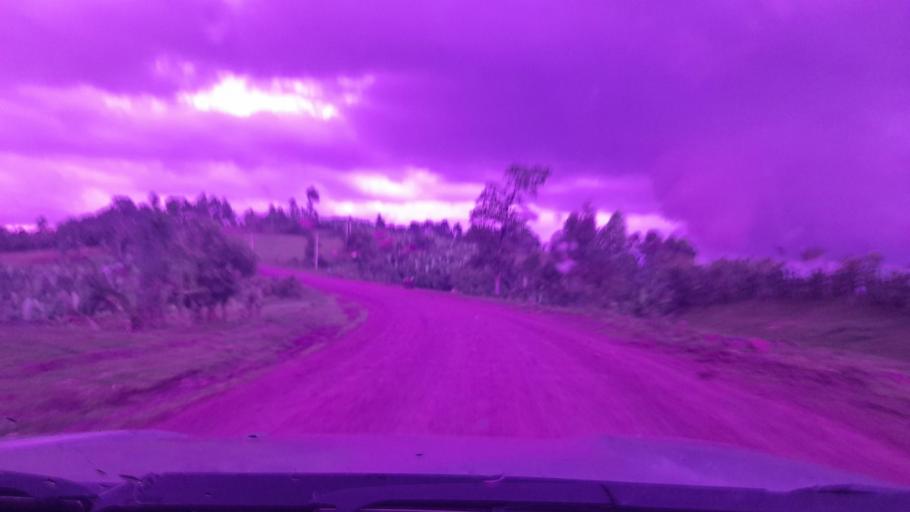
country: ET
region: Southern Nations, Nationalities, and People's Region
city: Mizan Teferi
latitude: 6.9077
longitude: 35.8429
